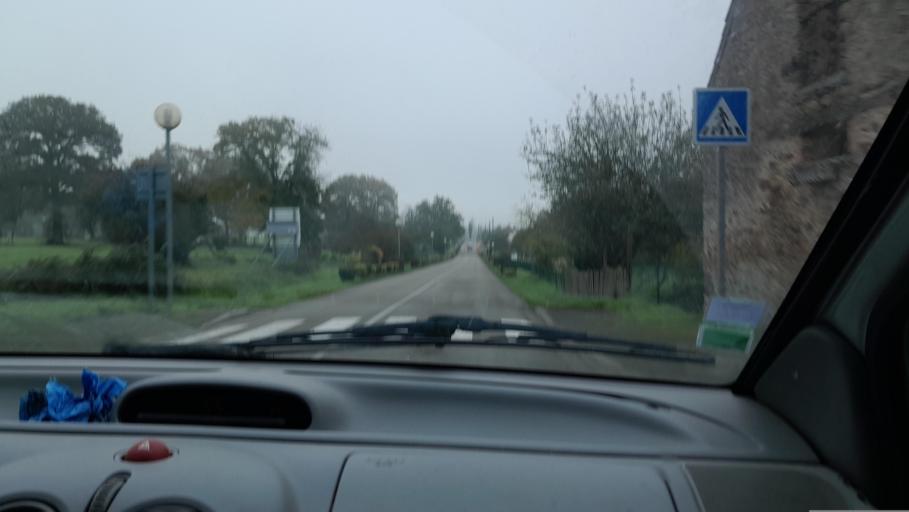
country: FR
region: Brittany
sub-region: Departement d'Ille-et-Vilaine
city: Le Pertre
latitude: 48.0010
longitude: -0.9704
